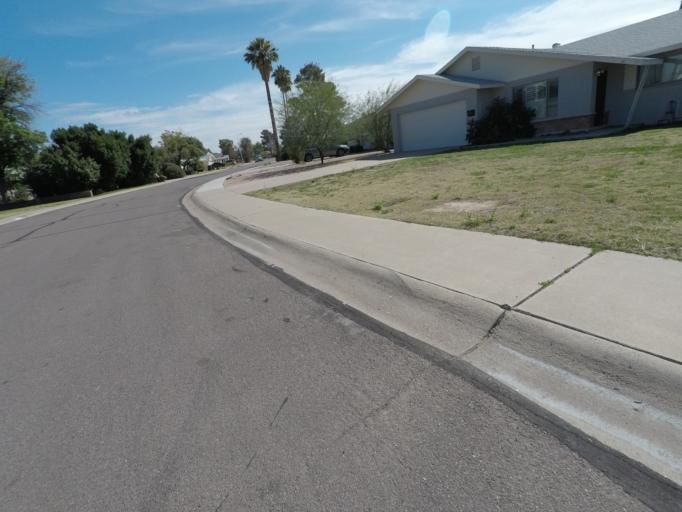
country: US
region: Arizona
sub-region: Maricopa County
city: Tempe Junction
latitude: 33.3969
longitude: -111.9425
